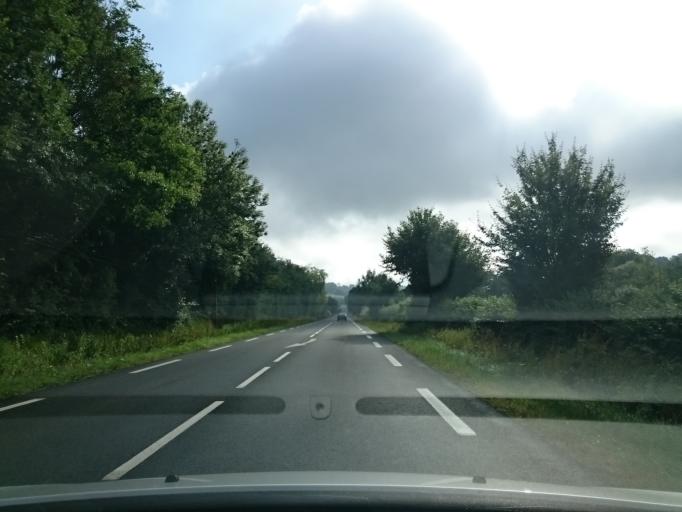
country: FR
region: Lower Normandy
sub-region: Departement du Calvados
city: Cambremer
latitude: 49.1238
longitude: 0.0781
